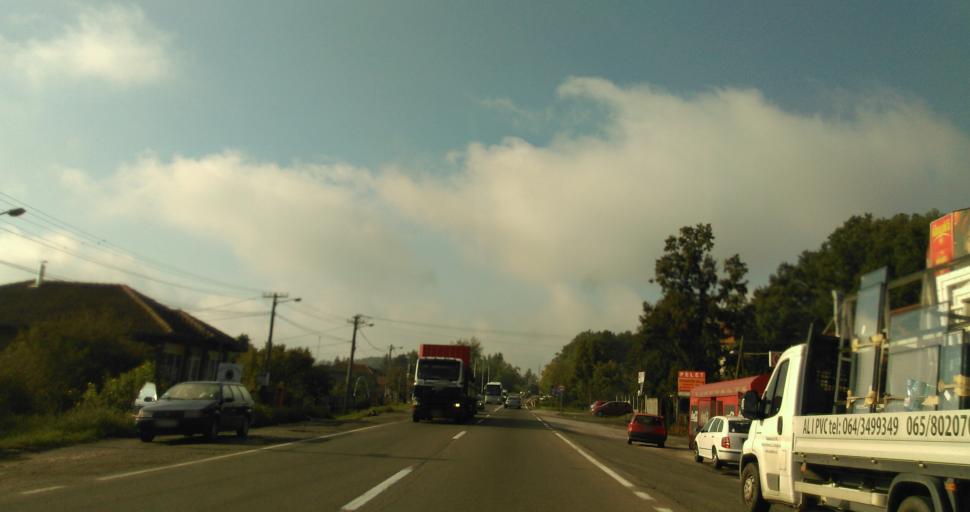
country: RS
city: Vranic
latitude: 44.6200
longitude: 20.3671
